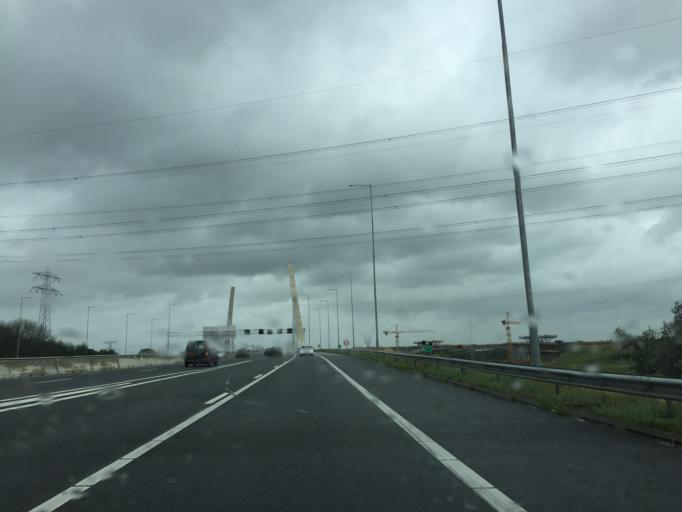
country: NL
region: North Holland
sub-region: Gemeente Amsterdam
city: Driemond
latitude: 52.3322
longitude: 5.0082
